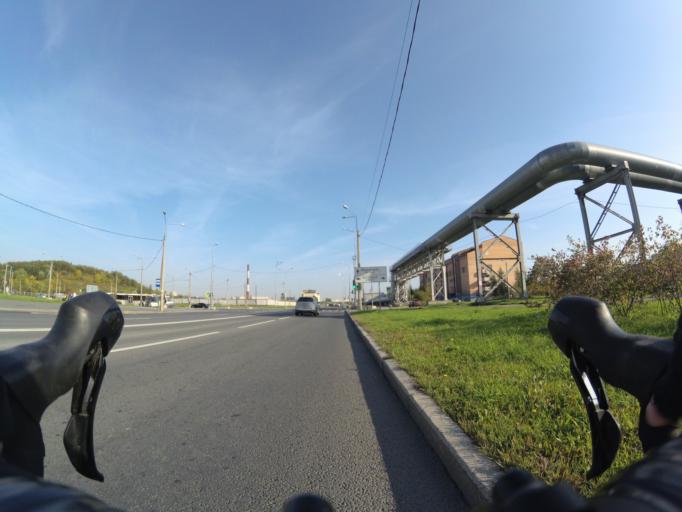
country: RU
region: Leningrad
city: Untolovo
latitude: 59.9940
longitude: 30.2178
